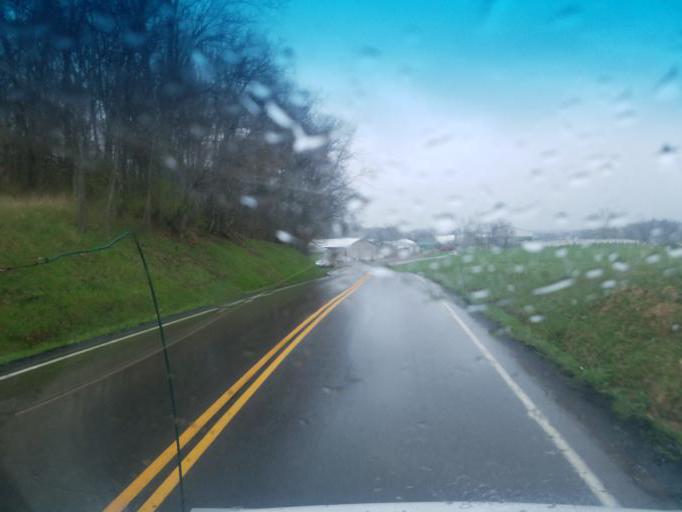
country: US
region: Ohio
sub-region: Holmes County
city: Millersburg
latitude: 40.6277
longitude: -81.9031
